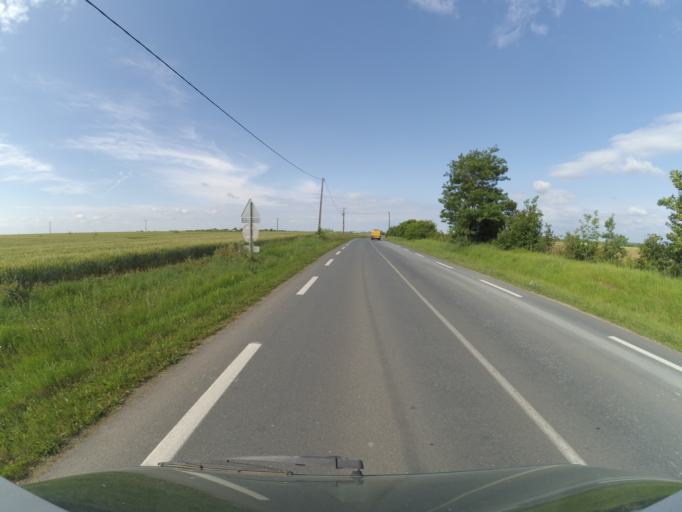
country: FR
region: Poitou-Charentes
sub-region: Departement de la Charente-Maritime
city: Saint-Xandre
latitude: 46.2240
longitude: -1.0845
